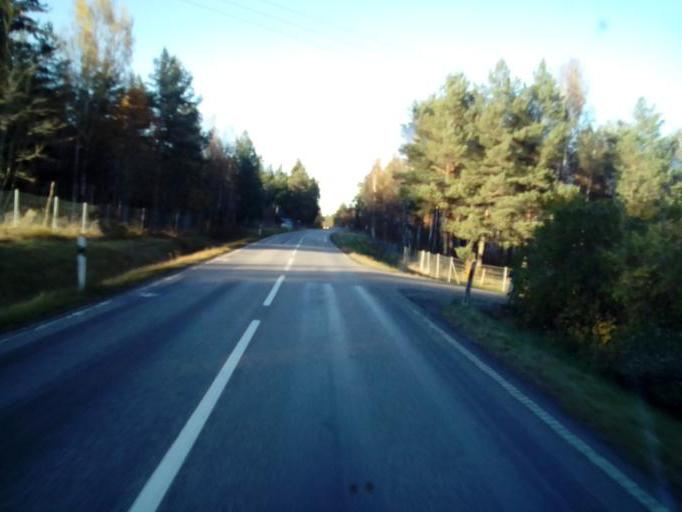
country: SE
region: OErebro
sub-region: Hallsbergs Kommun
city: Palsboda
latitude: 58.9070
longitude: 15.4350
